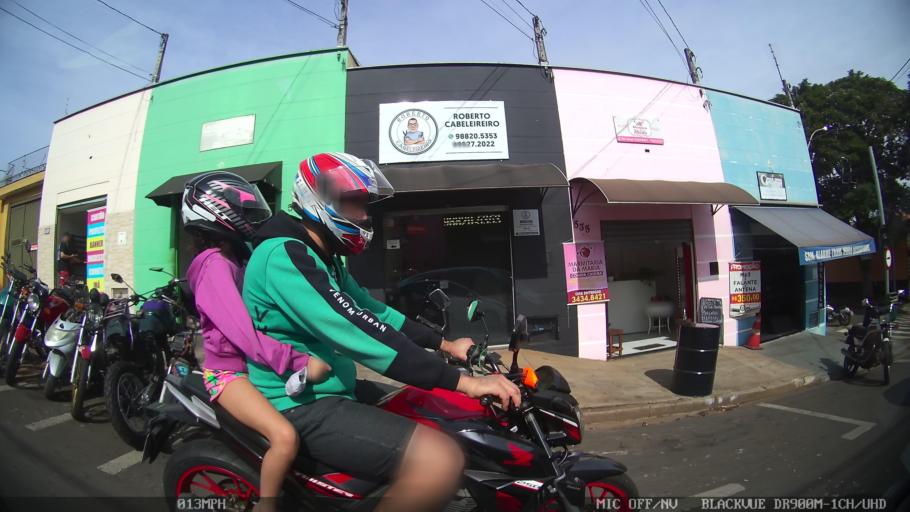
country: BR
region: Sao Paulo
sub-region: Piracicaba
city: Piracicaba
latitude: -22.7392
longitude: -47.6631
